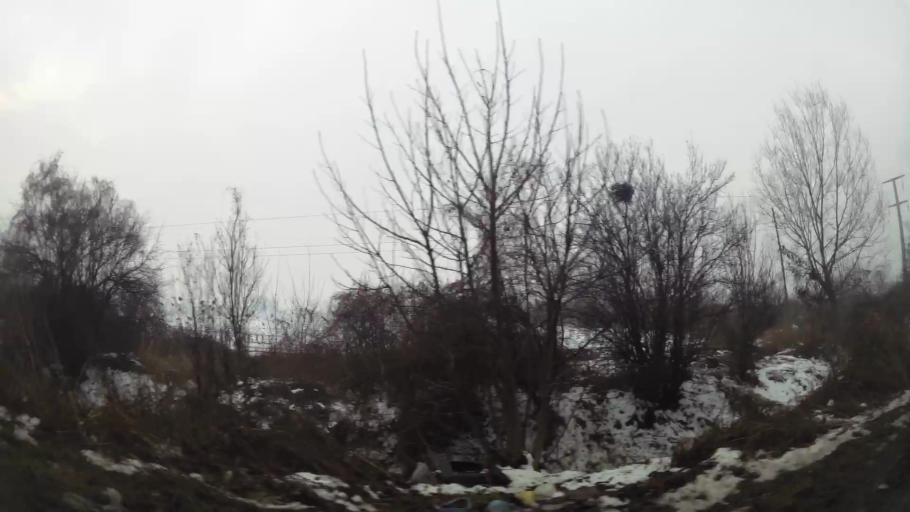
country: MK
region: Ilinden
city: Idrizovo
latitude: 41.9519
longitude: 21.5827
